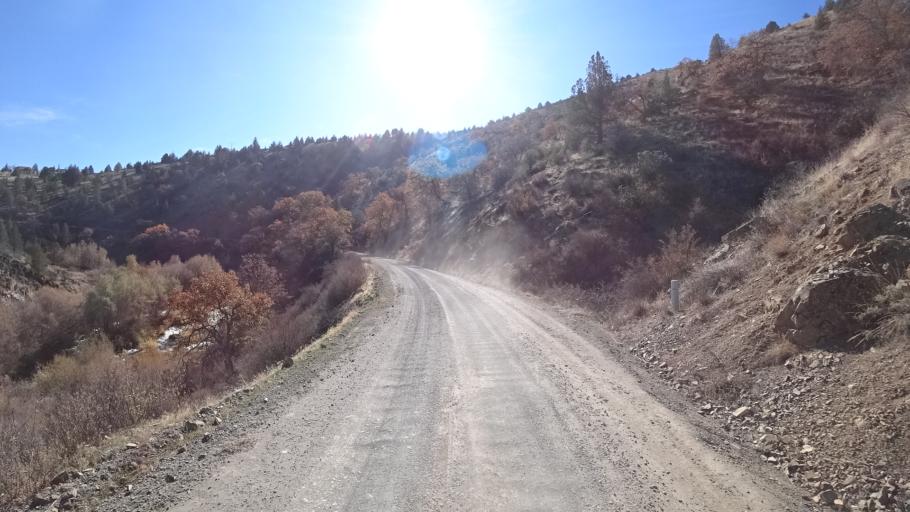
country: US
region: California
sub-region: Siskiyou County
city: Yreka
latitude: 41.7834
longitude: -122.6040
